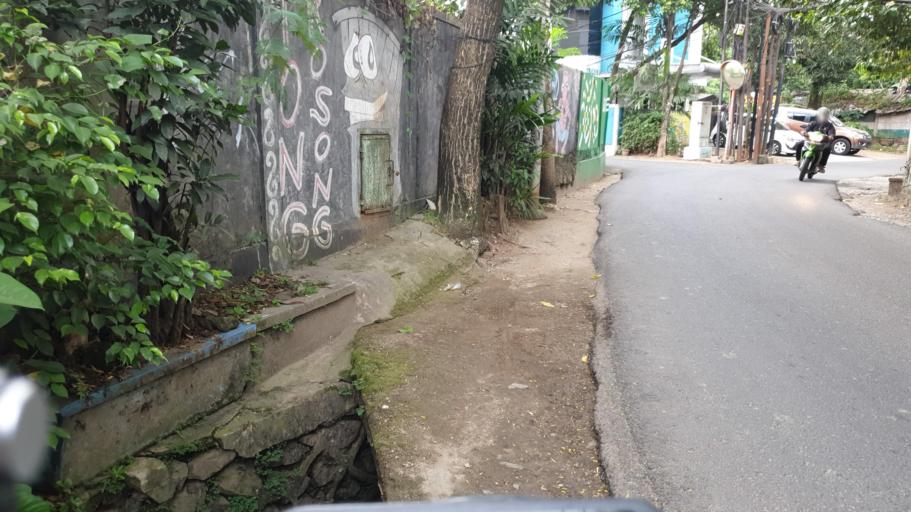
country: ID
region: Banten
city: South Tangerang
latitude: -6.2739
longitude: 106.7934
